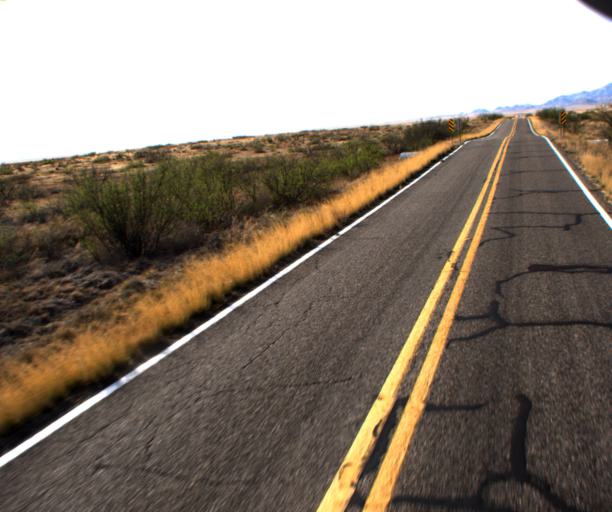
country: US
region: Arizona
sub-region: Cochise County
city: Willcox
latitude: 32.0523
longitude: -109.4932
